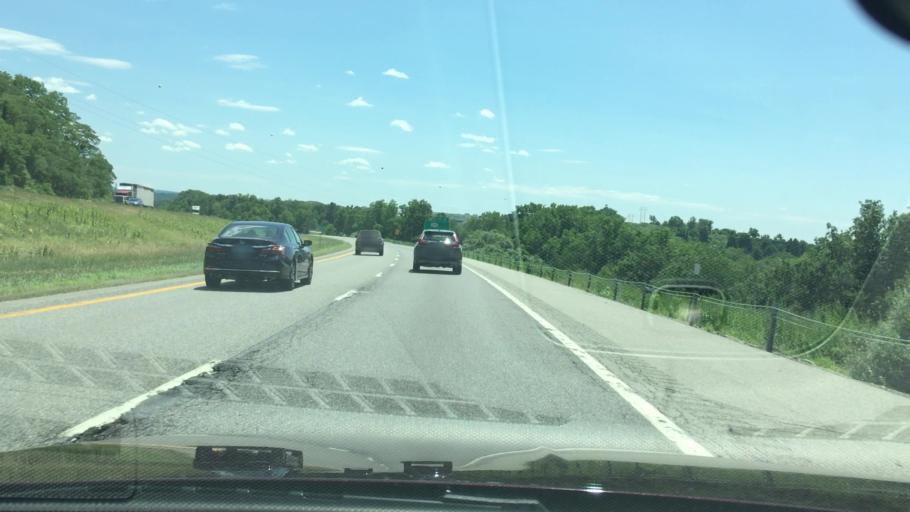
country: US
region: New York
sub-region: Putnam County
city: Brewster Hill
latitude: 41.4296
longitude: -73.6305
